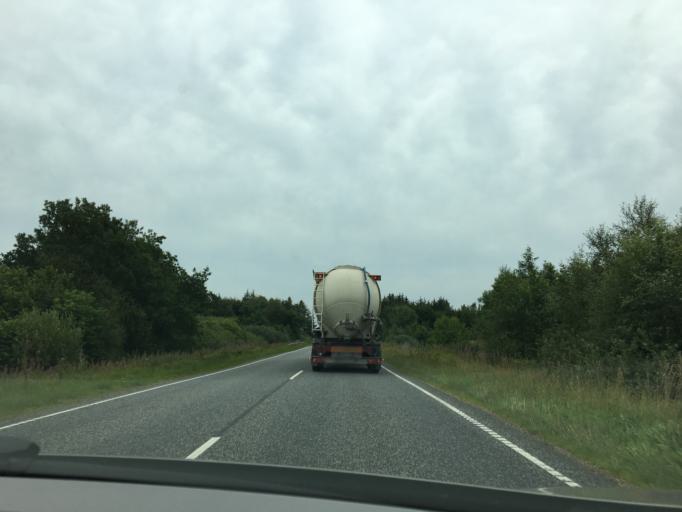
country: DK
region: Central Jutland
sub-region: Herning Kommune
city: Sunds
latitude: 56.2996
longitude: 8.9996
